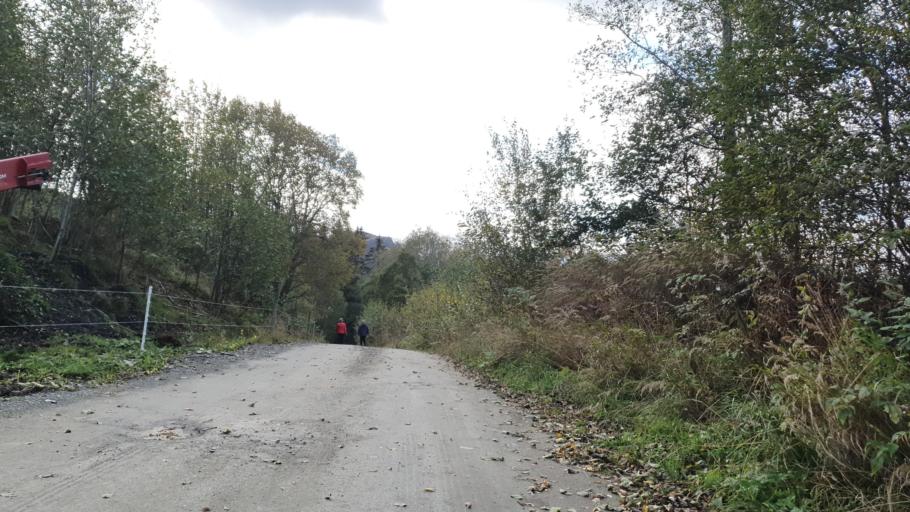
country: NO
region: Sor-Trondelag
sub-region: Klaebu
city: Klaebu
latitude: 63.2918
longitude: 10.4628
